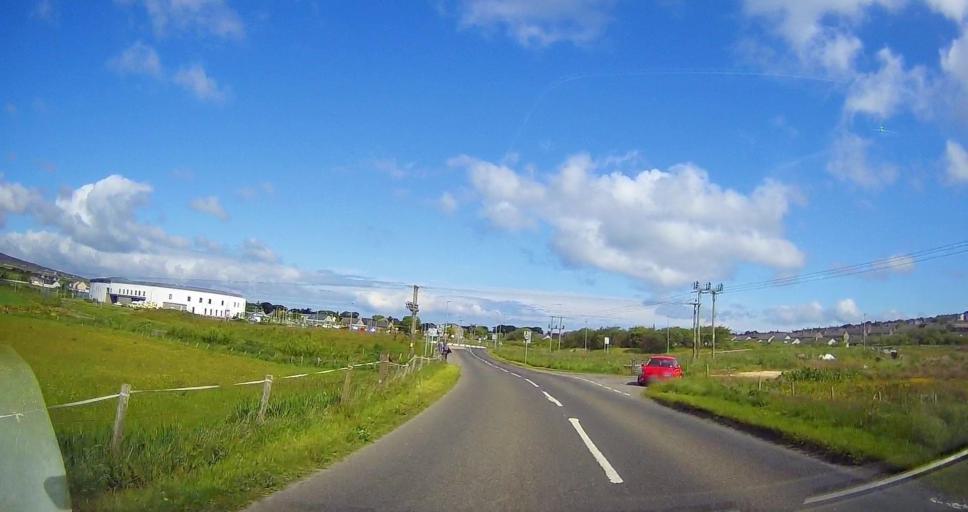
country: GB
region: Scotland
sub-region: Orkney Islands
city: Orkney
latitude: 58.9715
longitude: -2.9616
